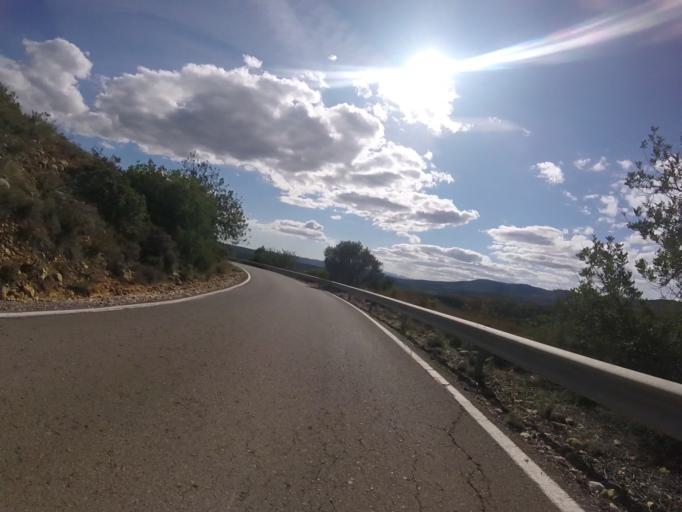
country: ES
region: Valencia
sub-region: Provincia de Castello
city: Cuevas de Vinroma
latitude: 40.3774
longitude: 0.1124
